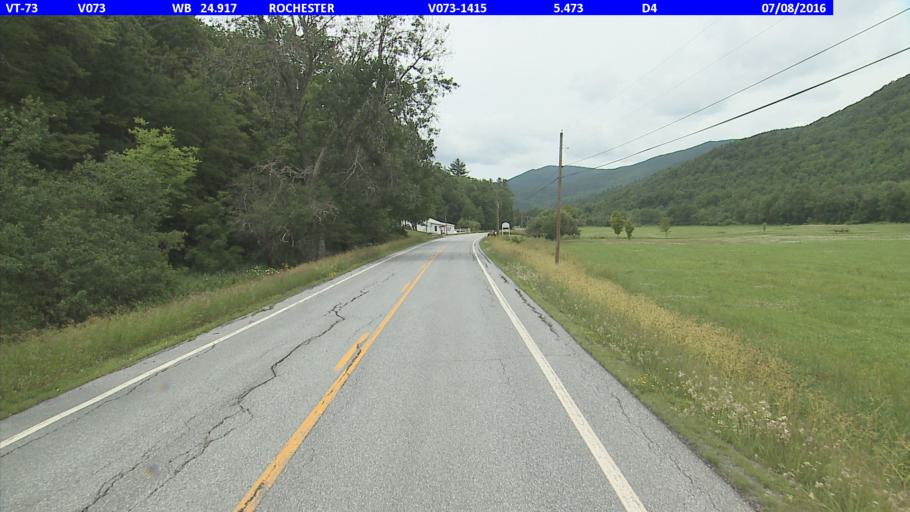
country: US
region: Vermont
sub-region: Orange County
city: Randolph
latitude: 43.8536
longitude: -72.8644
